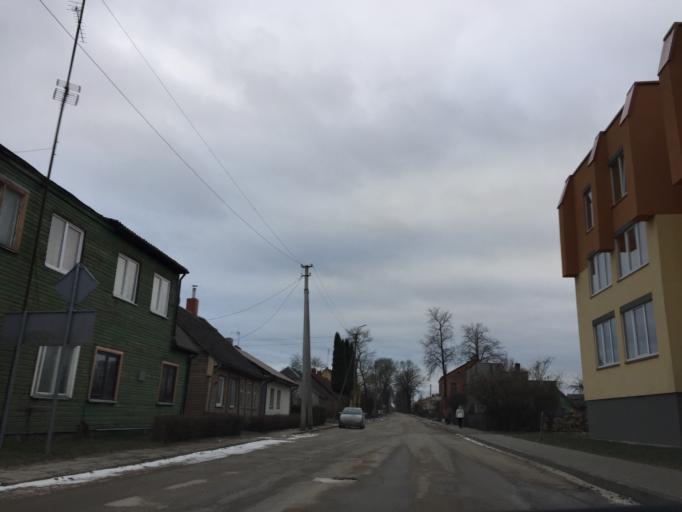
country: LT
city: Zagare
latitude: 56.3579
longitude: 23.2564
